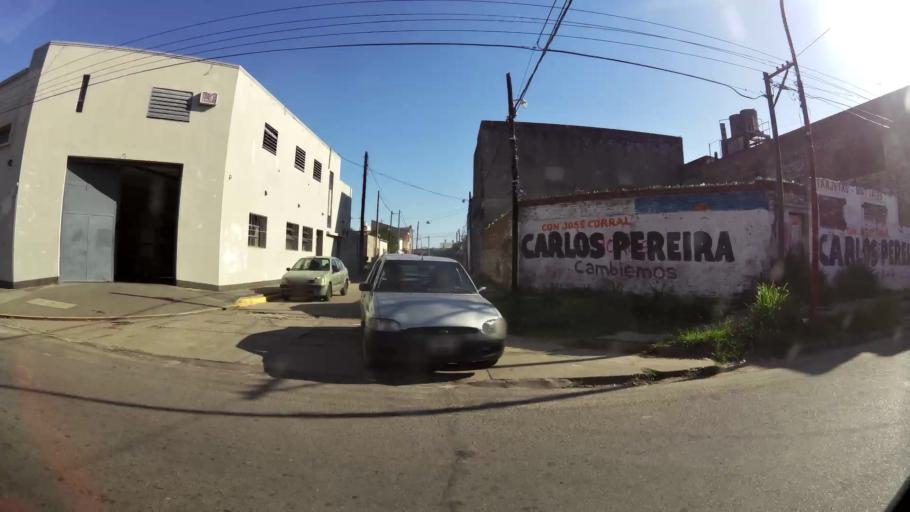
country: AR
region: Santa Fe
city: Santa Fe de la Vera Cruz
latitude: -31.6040
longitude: -60.7018
